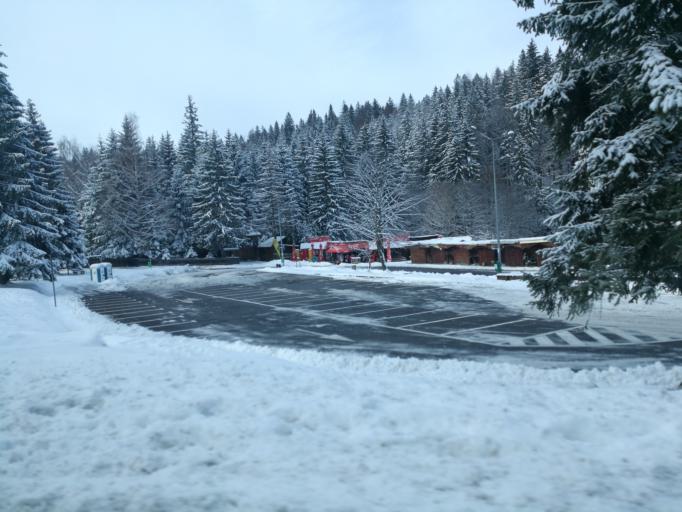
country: RO
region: Brasov
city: Brasov
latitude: 45.5914
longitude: 25.5505
